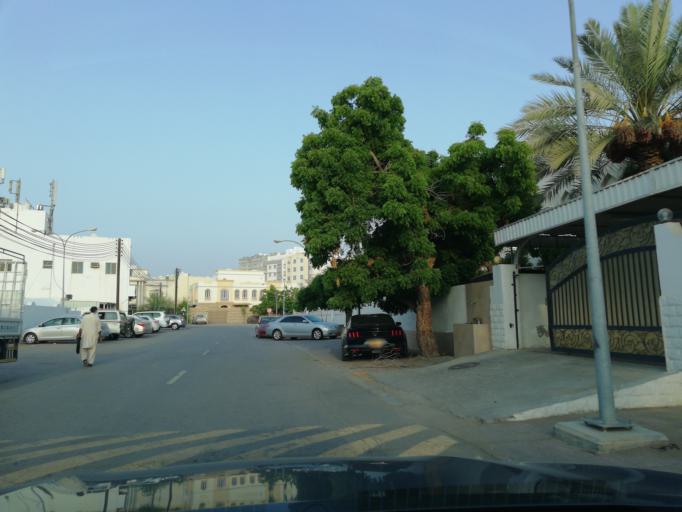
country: OM
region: Muhafazat Masqat
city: Bawshar
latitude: 23.5940
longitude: 58.3992
